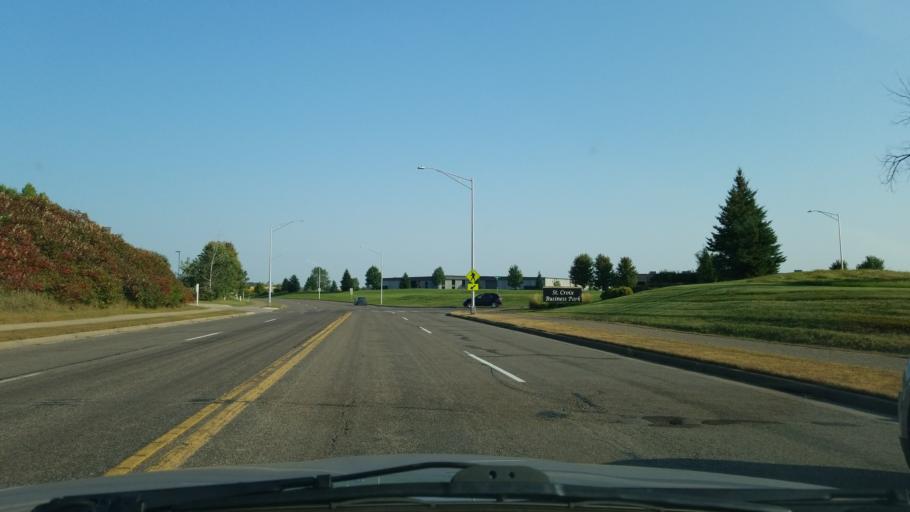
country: US
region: Wisconsin
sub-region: Saint Croix County
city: Hudson
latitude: 44.9506
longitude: -92.7108
